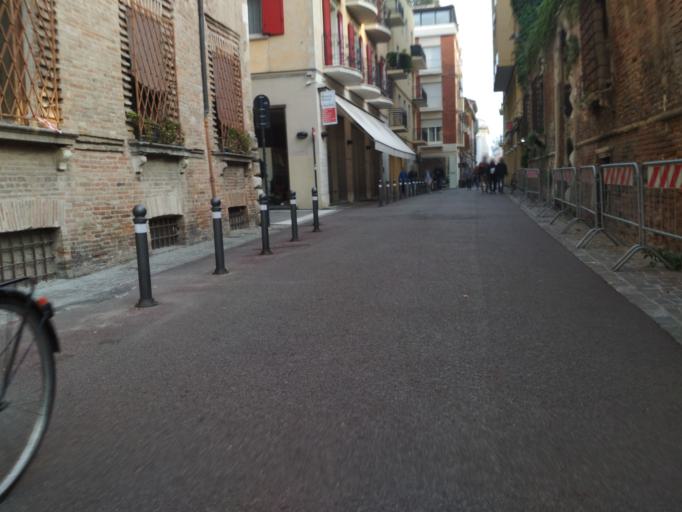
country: IT
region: Emilia-Romagna
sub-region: Provincia di Rimini
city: Rimini
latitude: 44.0609
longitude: 12.5687
